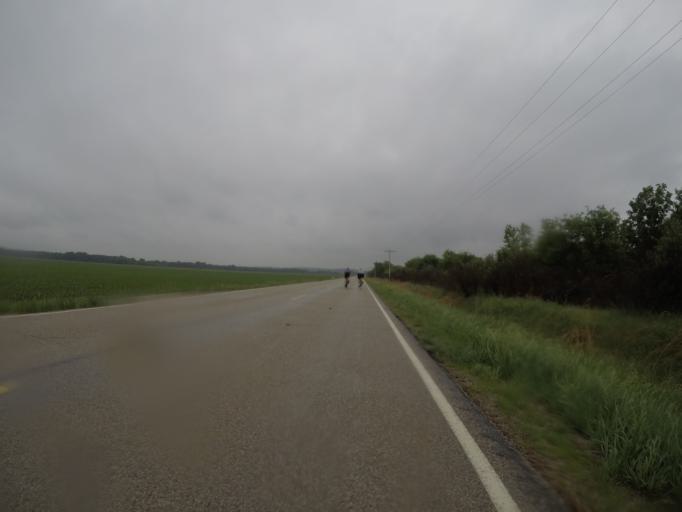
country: US
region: Kansas
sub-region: Pottawatomie County
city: Wamego
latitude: 39.3136
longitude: -96.2215
